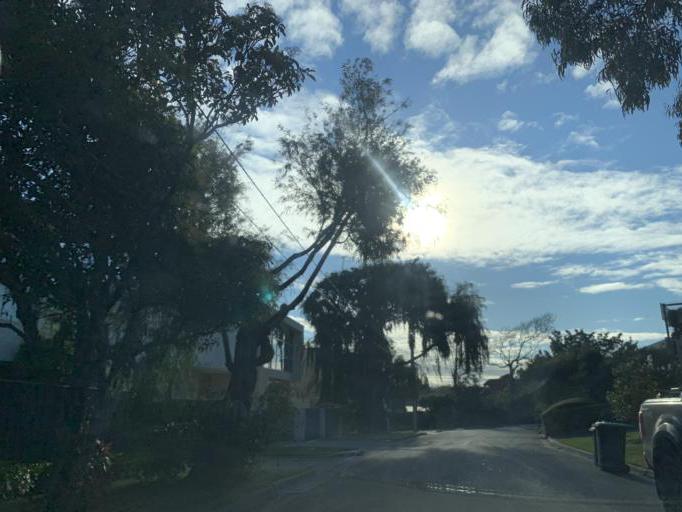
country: AU
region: Victoria
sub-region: Kingston
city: Mentone
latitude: -37.9861
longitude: 145.0573
